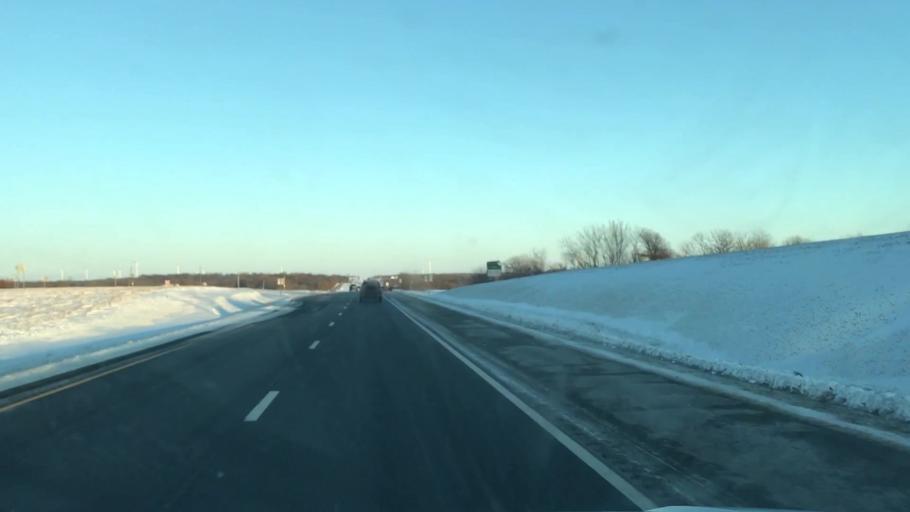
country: US
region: Missouri
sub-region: Clinton County
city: Gower
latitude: 39.7620
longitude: -94.4958
